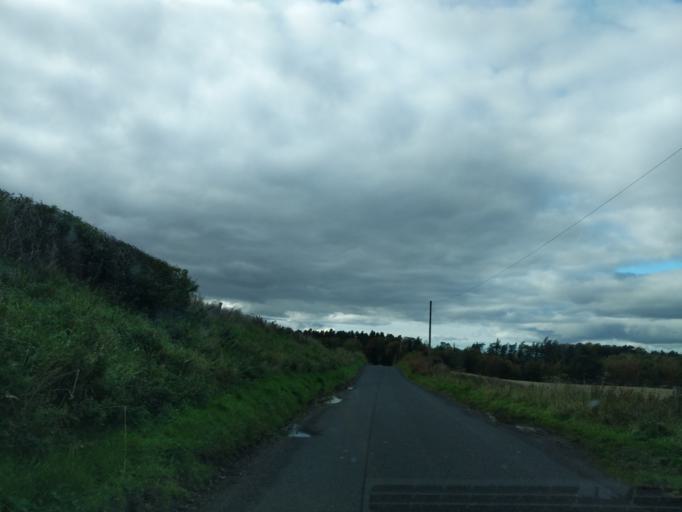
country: GB
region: Scotland
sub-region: East Lothian
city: Haddington
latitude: 55.9194
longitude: -2.7961
